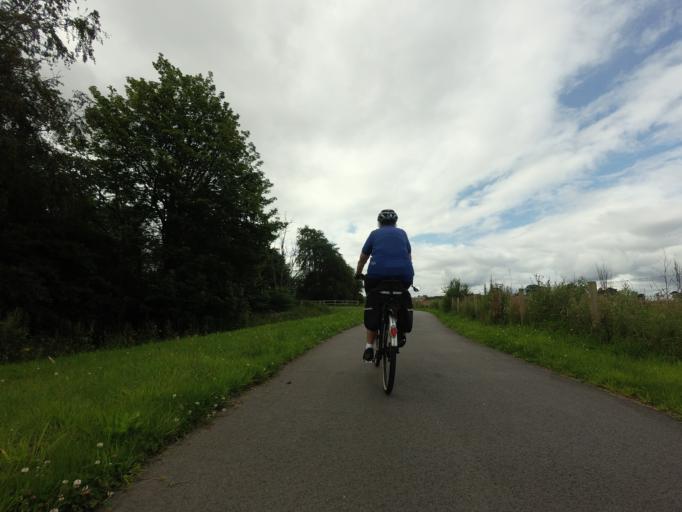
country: GB
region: Scotland
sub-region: Moray
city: Lhanbryd
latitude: 57.6423
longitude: -3.2632
